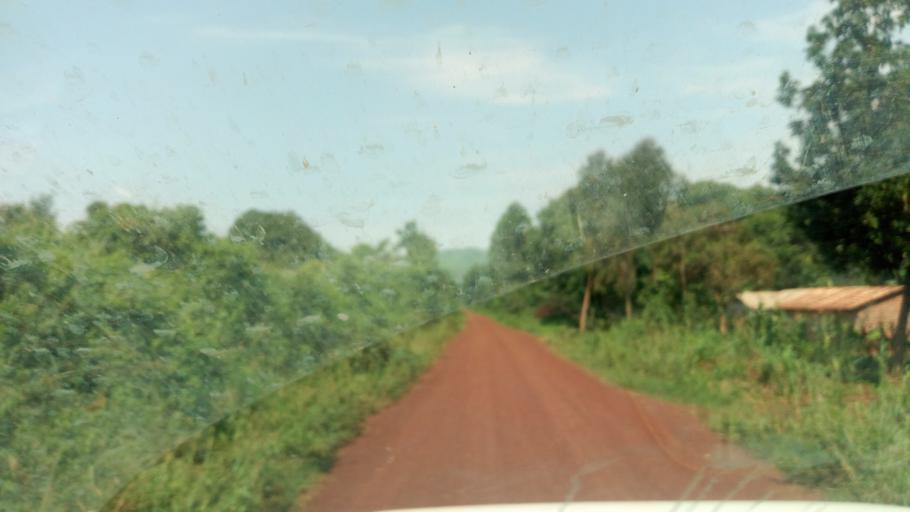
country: UG
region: Western Region
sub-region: Masindi District
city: Masindi
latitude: 1.6630
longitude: 31.8137
